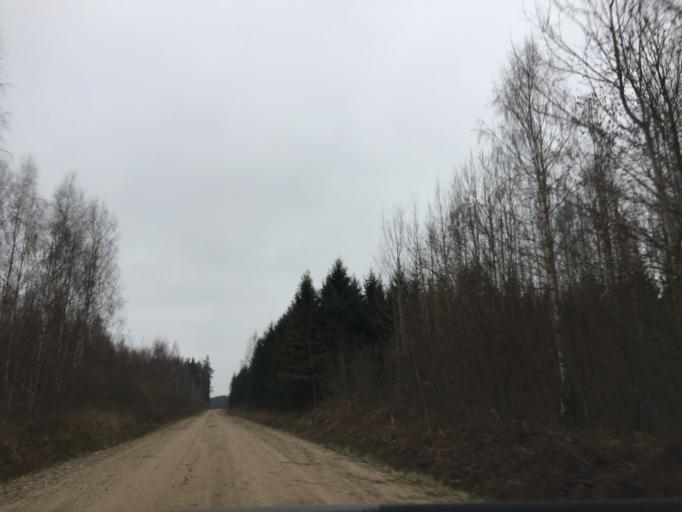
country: LV
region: Limbazu Rajons
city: Limbazi
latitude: 57.4744
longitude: 24.7544
